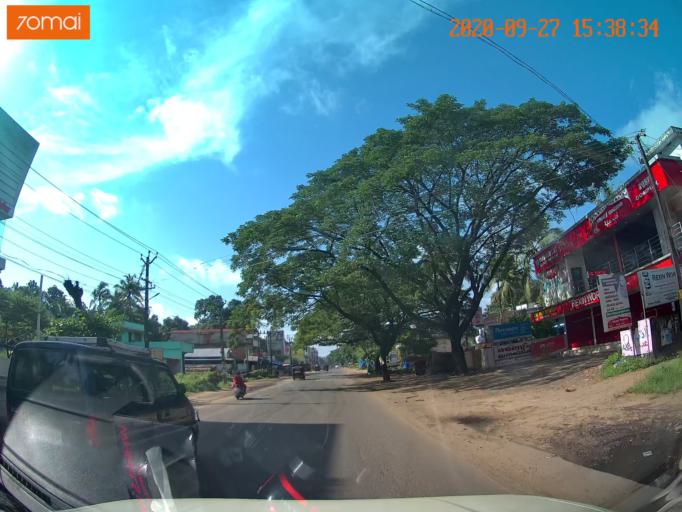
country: IN
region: Kerala
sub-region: Thrissur District
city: Thanniyam
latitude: 10.4632
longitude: 76.0835
